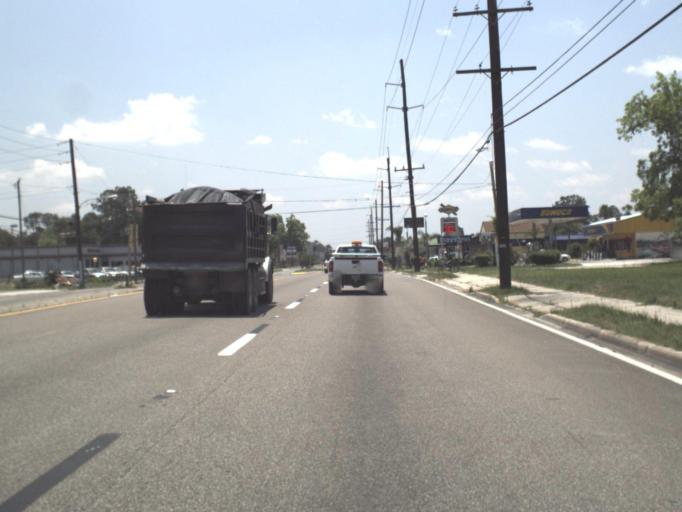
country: US
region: Florida
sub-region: Bradford County
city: Starke
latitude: 29.9575
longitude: -82.1069
